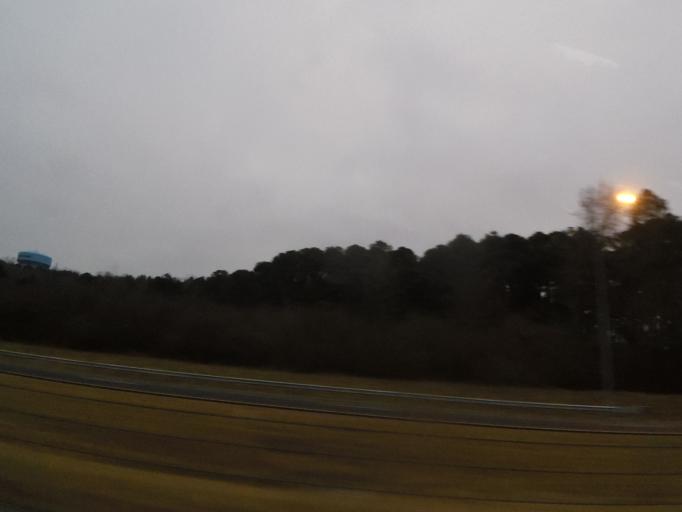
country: US
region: Alabama
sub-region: Cullman County
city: Cullman
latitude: 34.1747
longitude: -86.8761
